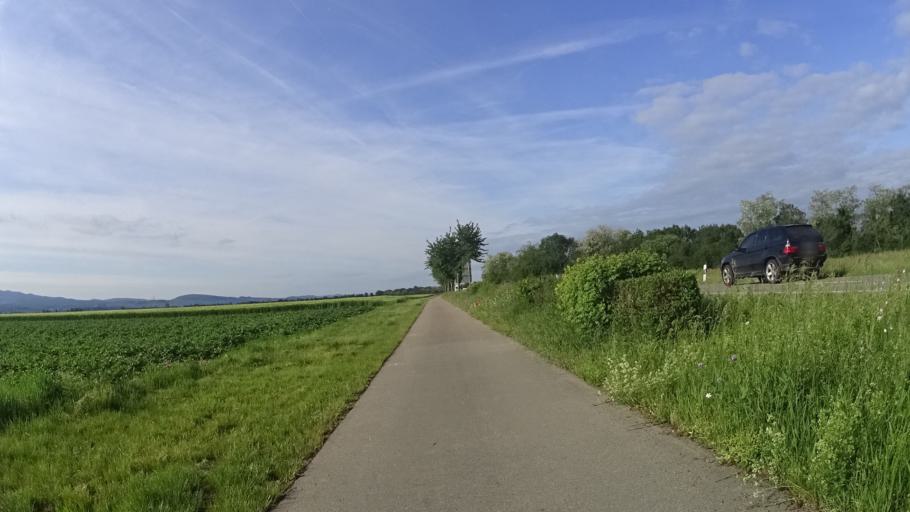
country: FR
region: Alsace
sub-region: Departement du Haut-Rhin
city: Blodelsheim
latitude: 47.8631
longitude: 7.5862
